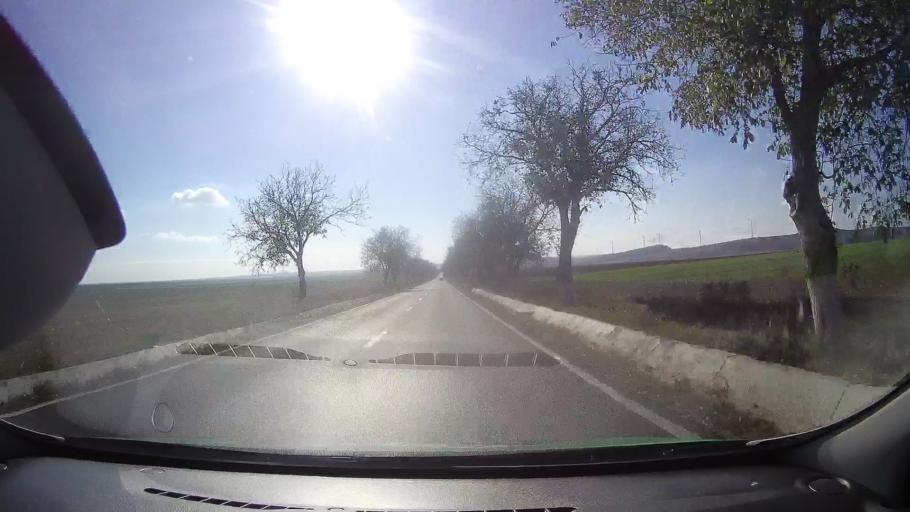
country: RO
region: Tulcea
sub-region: Comuna Ceamurlia de Jos
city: Ceamurlia de Jos
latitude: 44.8018
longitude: 28.6906
